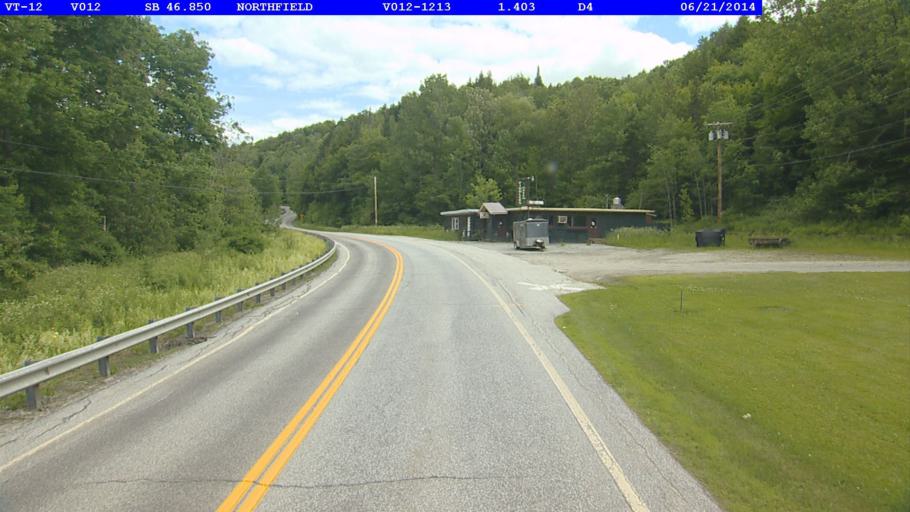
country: US
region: Vermont
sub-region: Washington County
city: Northfield
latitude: 44.1105
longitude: -72.6502
